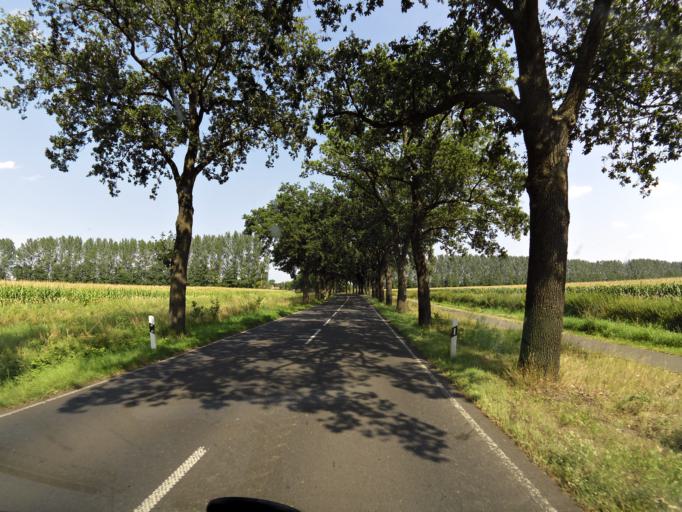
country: DE
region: Brandenburg
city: Liebenwalde
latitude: 52.8746
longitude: 13.3411
